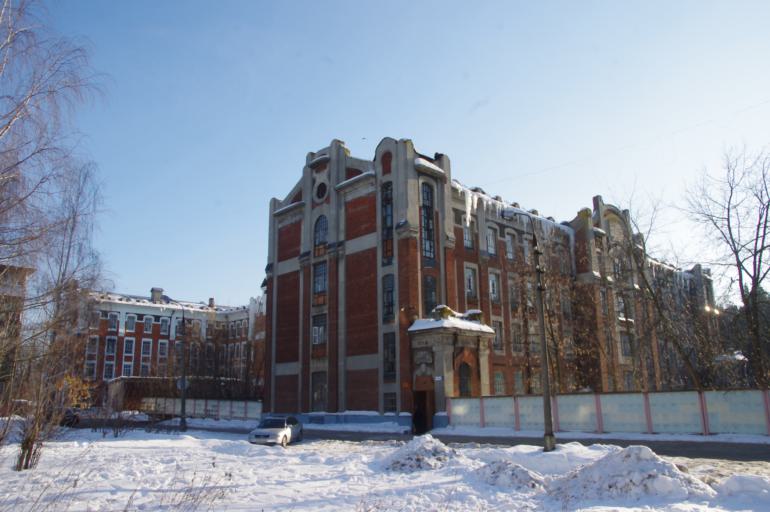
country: RU
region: Moskovskaya
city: Noginsk
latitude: 55.8806
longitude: 38.4512
